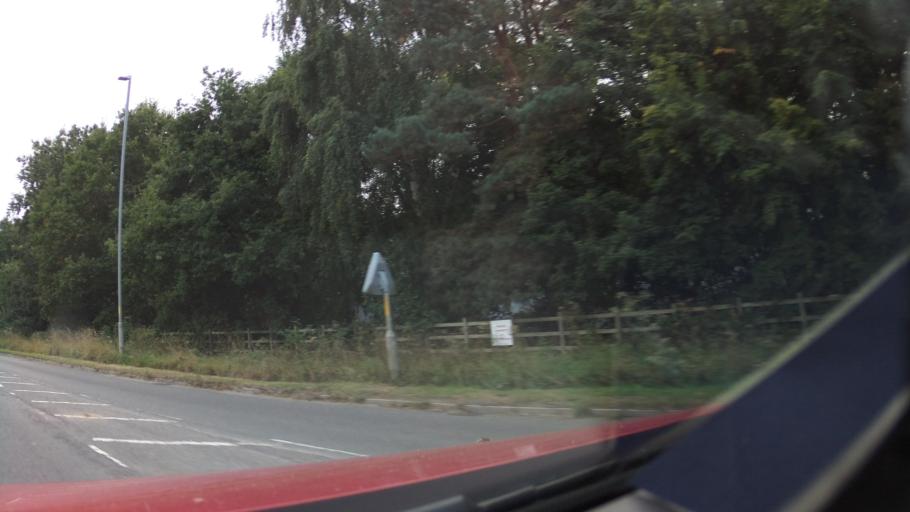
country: GB
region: England
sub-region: Nottinghamshire
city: South Collingham
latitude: 53.1499
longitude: -0.6700
